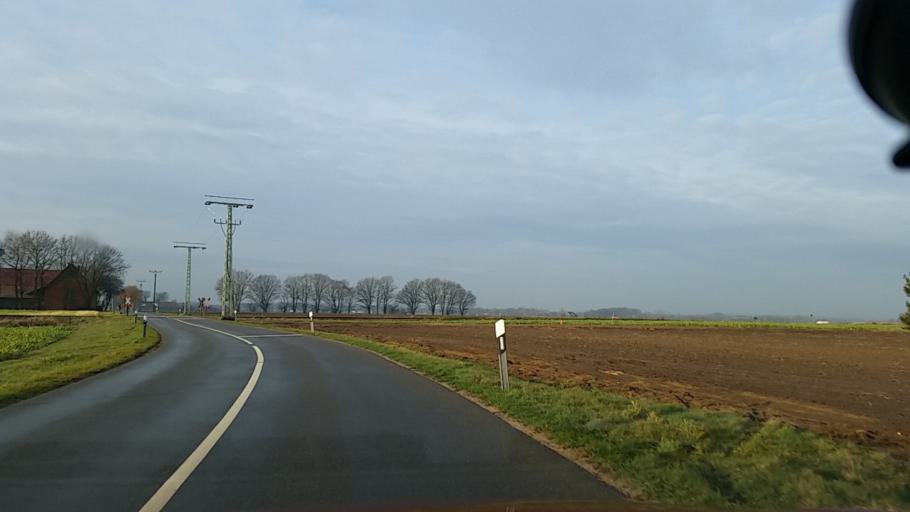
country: DE
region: Lower Saxony
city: Luder
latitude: 52.8045
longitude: 10.6925
